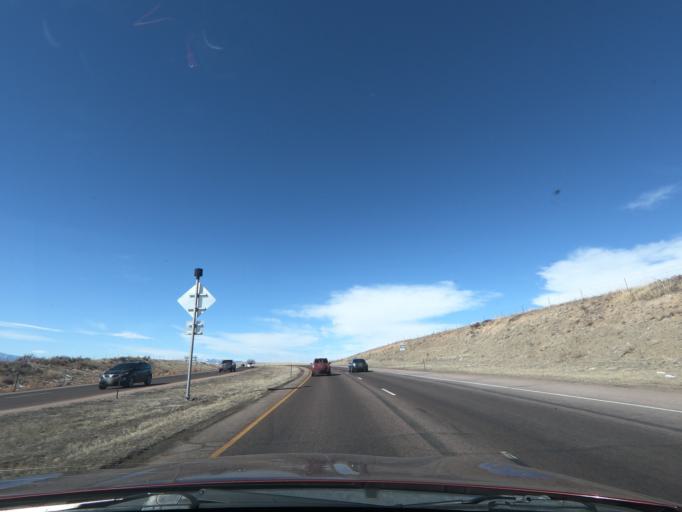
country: US
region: Colorado
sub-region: El Paso County
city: Security-Widefield
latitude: 38.7630
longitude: -104.6834
